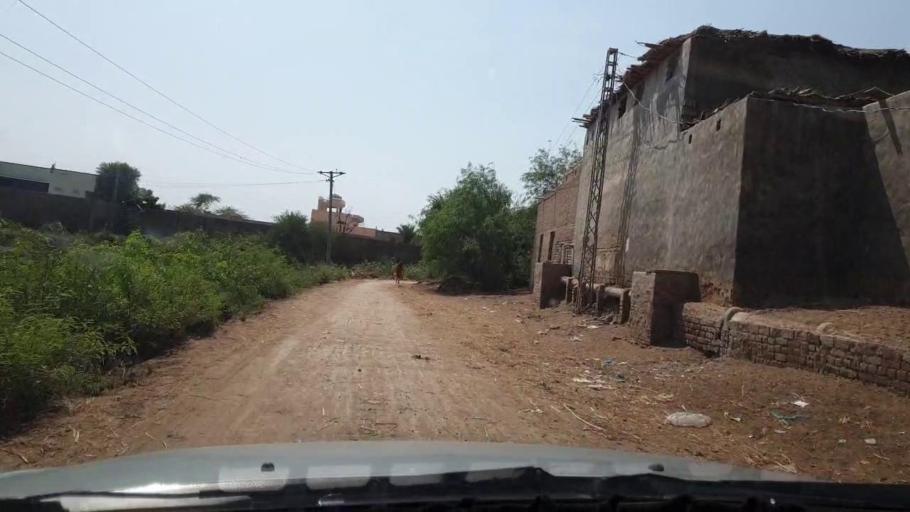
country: PK
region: Sindh
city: Tando Muhammad Khan
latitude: 25.1231
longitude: 68.6205
